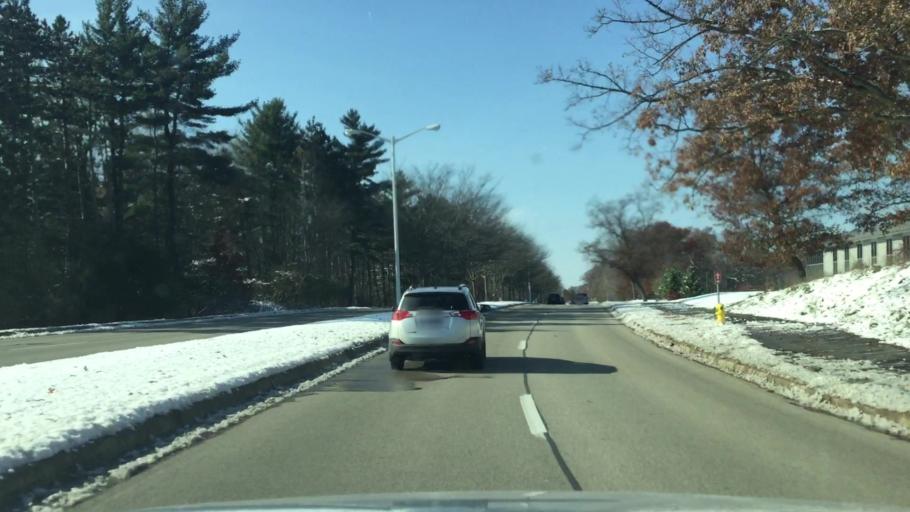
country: US
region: Michigan
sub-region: Kalamazoo County
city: Portage
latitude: 42.2155
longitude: -85.5662
